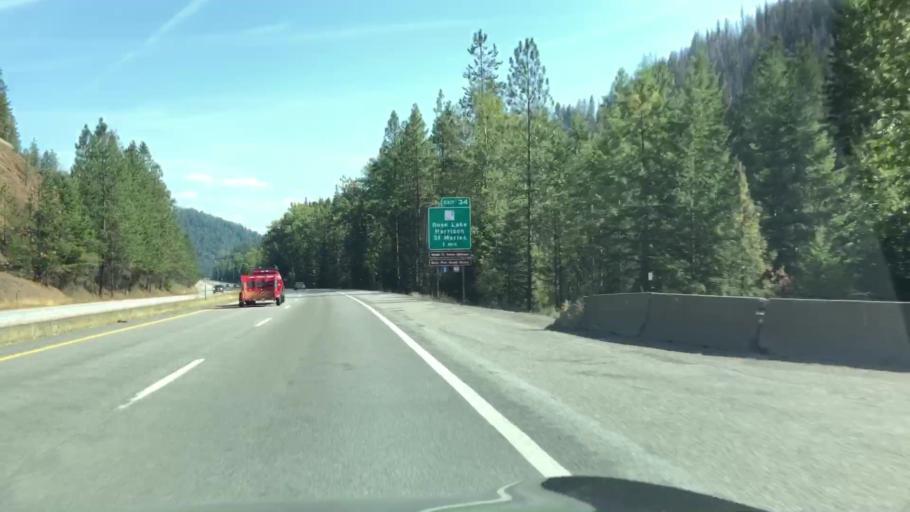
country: US
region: Idaho
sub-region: Shoshone County
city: Pinehurst
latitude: 47.5827
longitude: -116.4677
